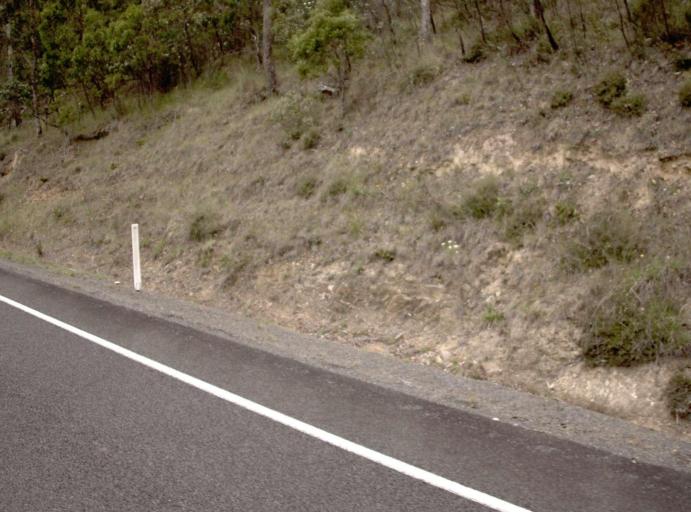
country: AU
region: New South Wales
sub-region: Bombala
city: Bombala
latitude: -37.2636
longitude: 149.2349
